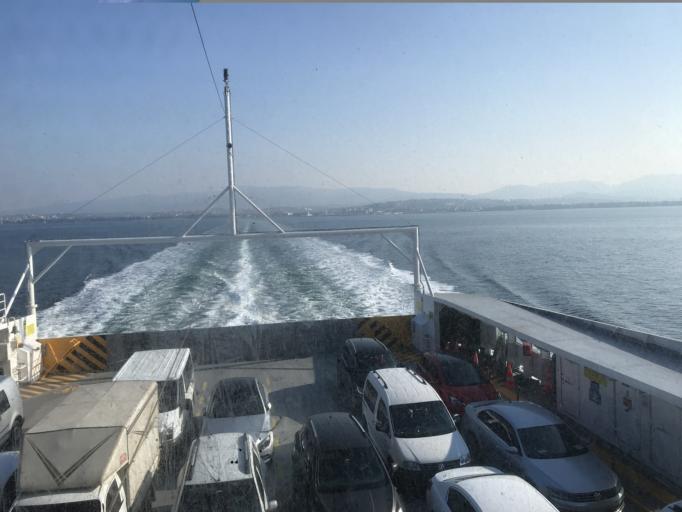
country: TR
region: Yalova
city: Yalova
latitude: 40.6832
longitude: 29.2628
